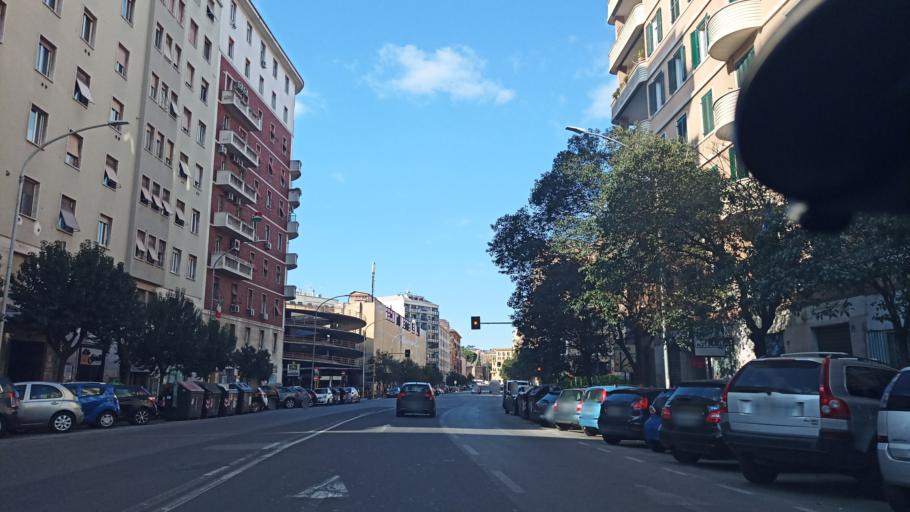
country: IT
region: Latium
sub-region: Citta metropolitana di Roma Capitale
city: Rome
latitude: 41.8815
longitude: 12.5082
